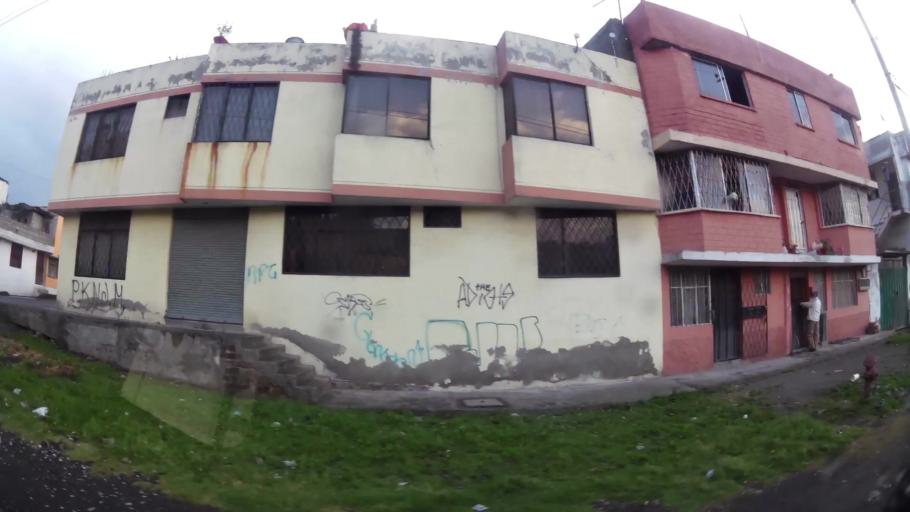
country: EC
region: Pichincha
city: Quito
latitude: -0.2989
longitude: -78.5381
